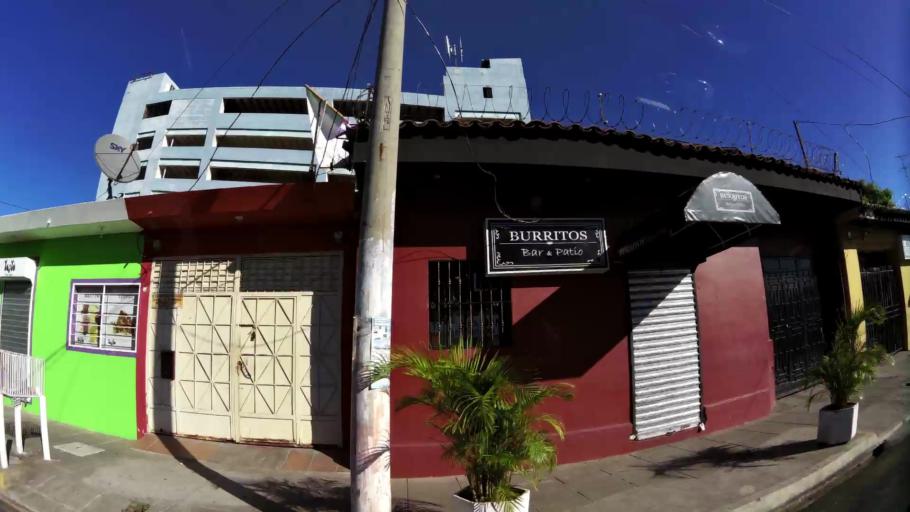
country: SV
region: San Miguel
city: San Miguel
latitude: 13.4781
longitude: -88.1823
